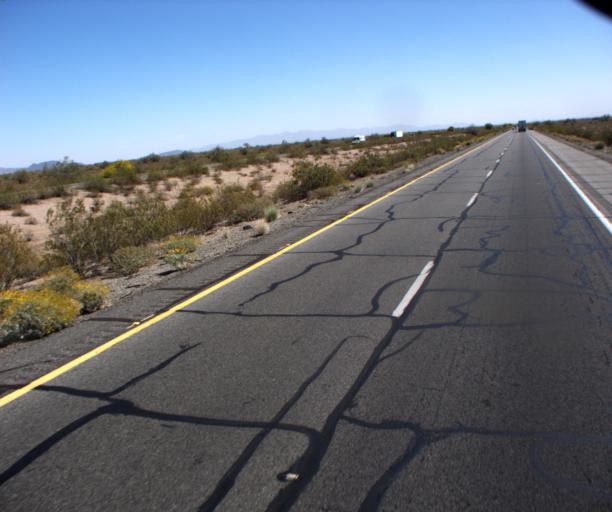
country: US
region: Arizona
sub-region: Maricopa County
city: Buckeye
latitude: 33.5127
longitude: -113.0247
